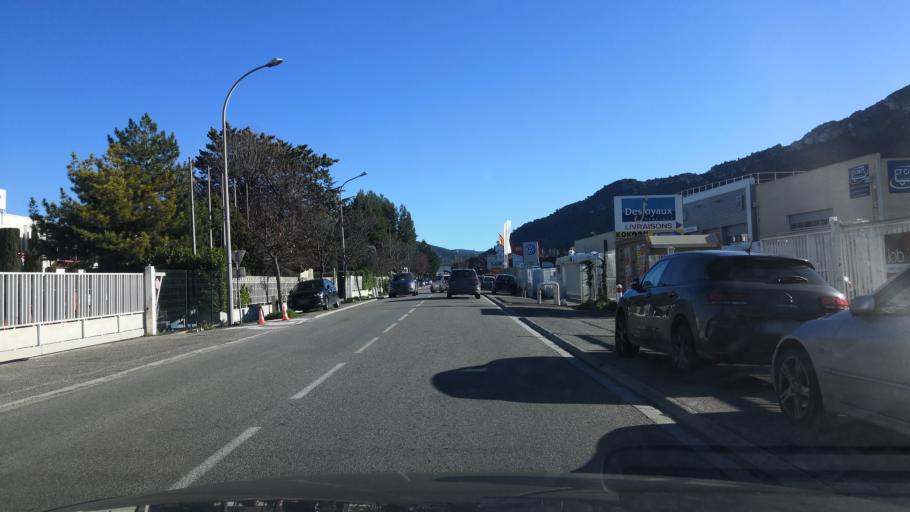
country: FR
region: Provence-Alpes-Cote d'Azur
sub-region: Departement des Bouches-du-Rhone
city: Gemenos
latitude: 43.2833
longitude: 5.6053
